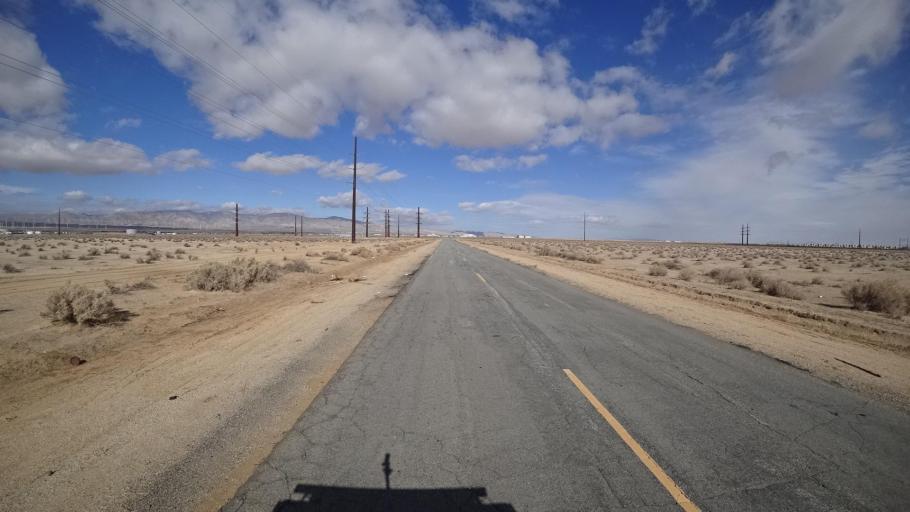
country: US
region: California
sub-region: Kern County
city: Mojave
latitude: 35.0217
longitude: -118.1496
